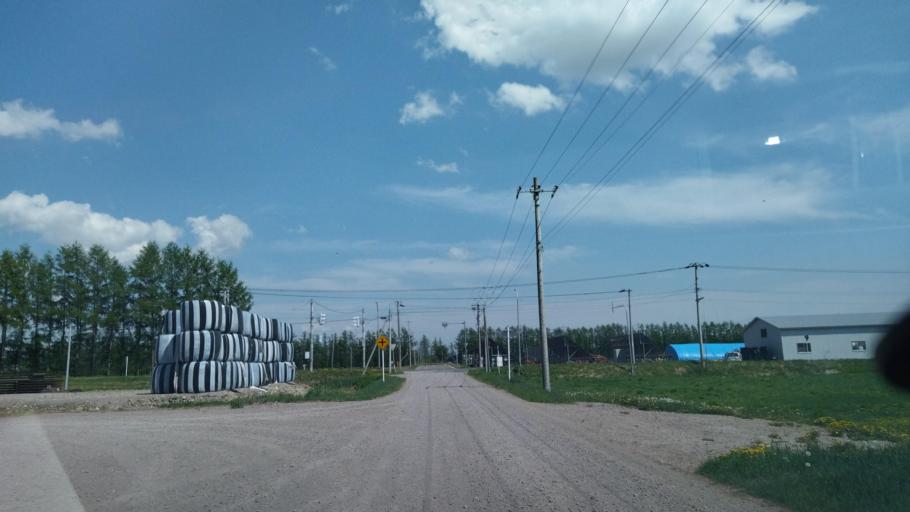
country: JP
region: Hokkaido
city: Otofuke
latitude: 43.1313
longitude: 143.2235
